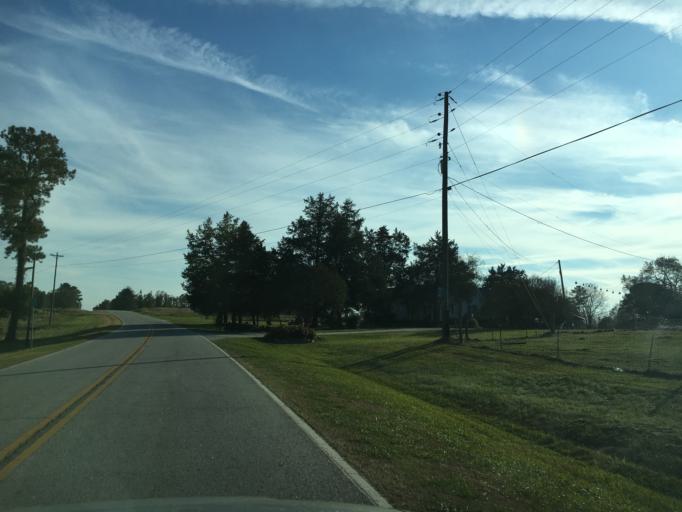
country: US
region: Georgia
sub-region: Elbert County
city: Elberton
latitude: 34.0015
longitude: -82.7809
